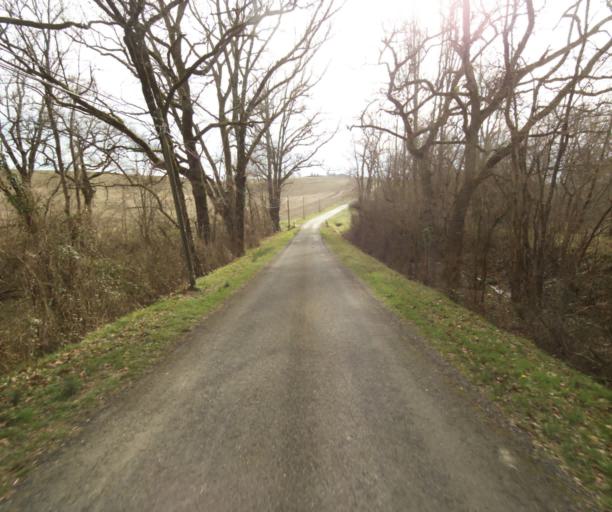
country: FR
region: Aquitaine
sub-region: Departement des Landes
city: Gabarret
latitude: 43.9424
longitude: 0.0465
